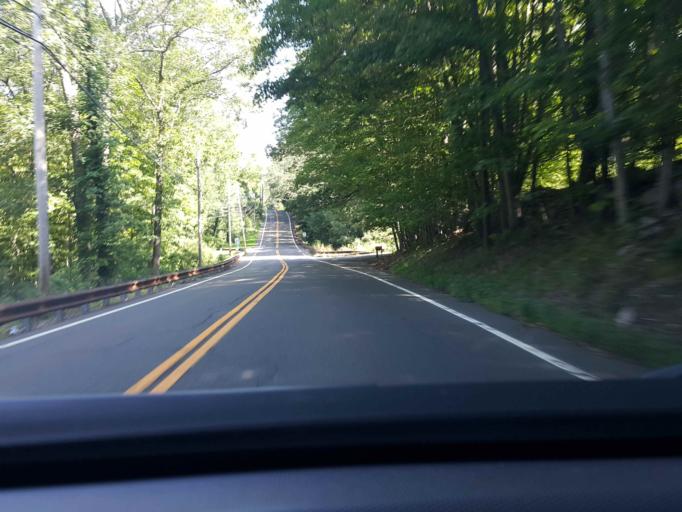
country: US
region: Connecticut
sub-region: New Haven County
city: North Branford
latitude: 41.3559
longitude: -72.7207
